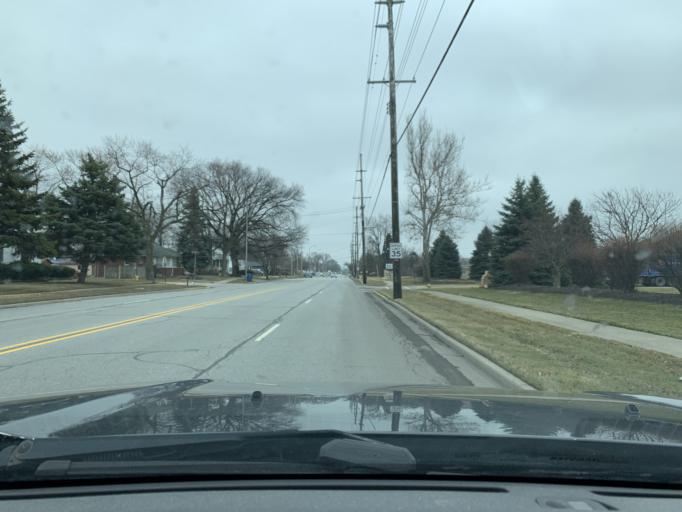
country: US
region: Indiana
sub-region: Lake County
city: Highland
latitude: 41.5417
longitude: -87.4616
